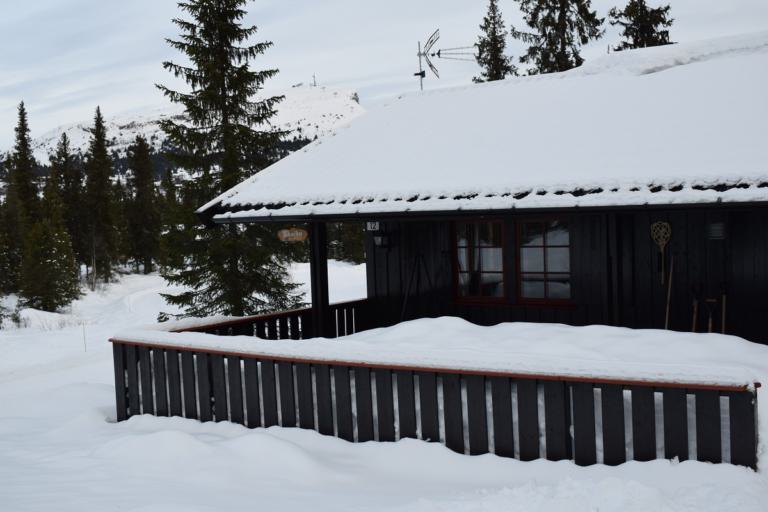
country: NO
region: Oppland
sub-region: Gausdal
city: Segalstad bru
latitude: 61.3303
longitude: 10.0724
